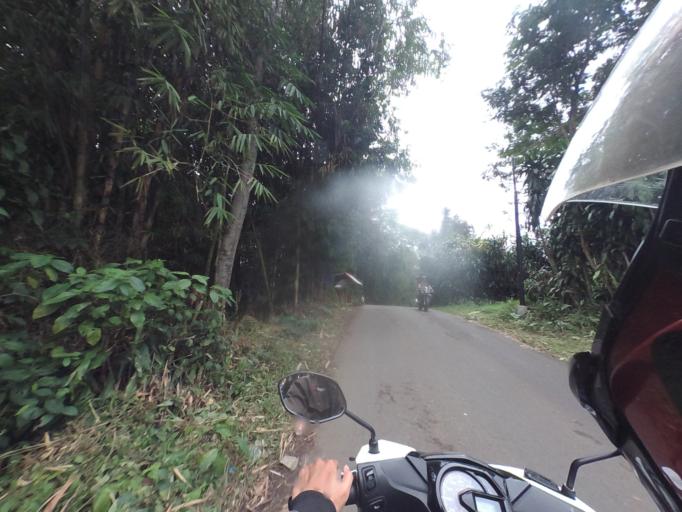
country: ID
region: West Java
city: Bogor
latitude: -6.6379
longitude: 106.7426
